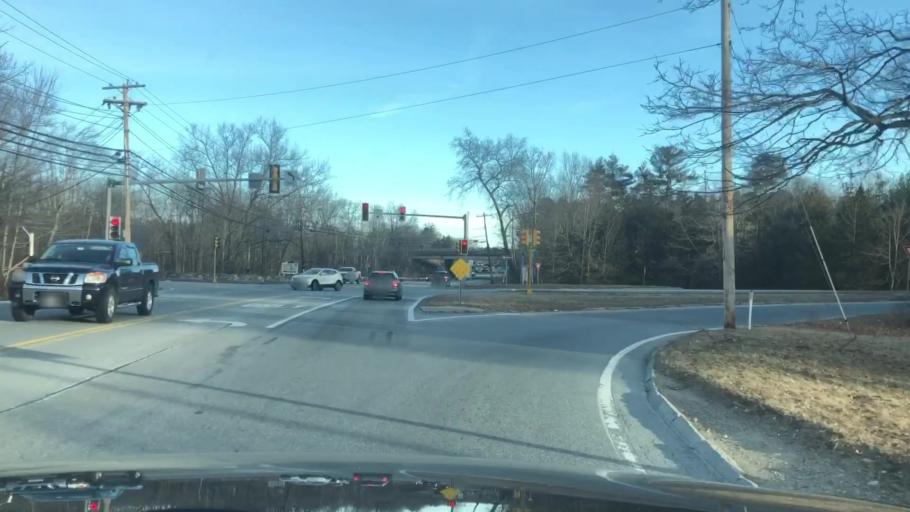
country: US
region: Massachusetts
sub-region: Worcester County
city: Bolton
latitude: 42.4313
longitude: -71.5956
